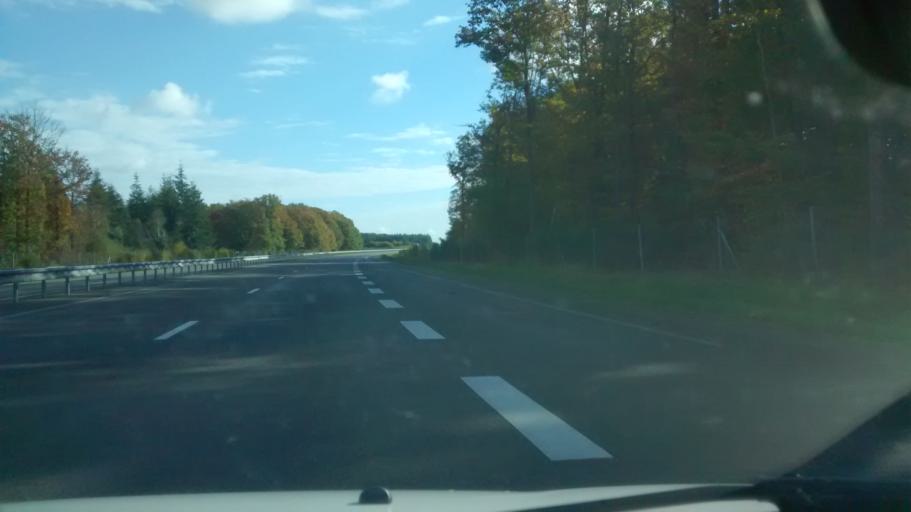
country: FR
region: Pays de la Loire
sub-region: Departement de Maine-et-Loire
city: Combree
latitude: 47.7303
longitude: -1.0700
